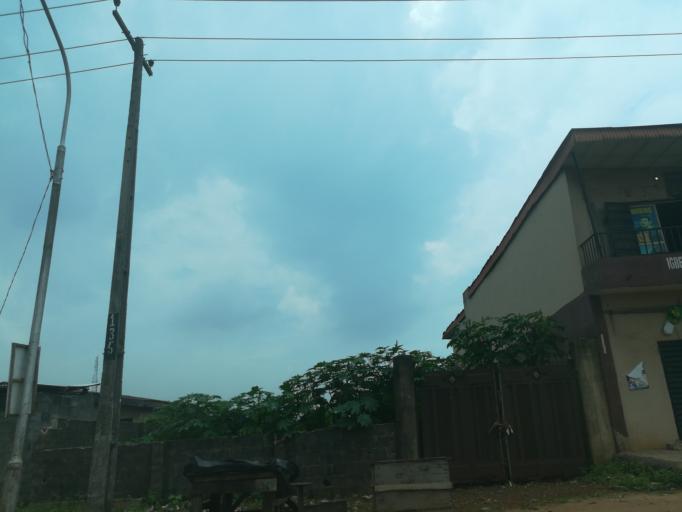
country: NG
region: Lagos
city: Ikorodu
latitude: 6.5675
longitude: 3.5916
